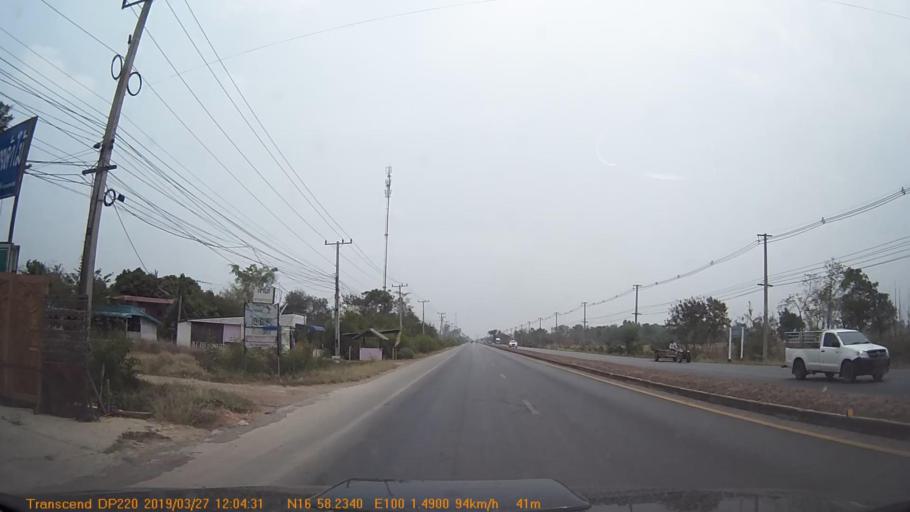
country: TH
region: Sukhothai
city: Kong Krailat
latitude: 16.9705
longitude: 100.0253
